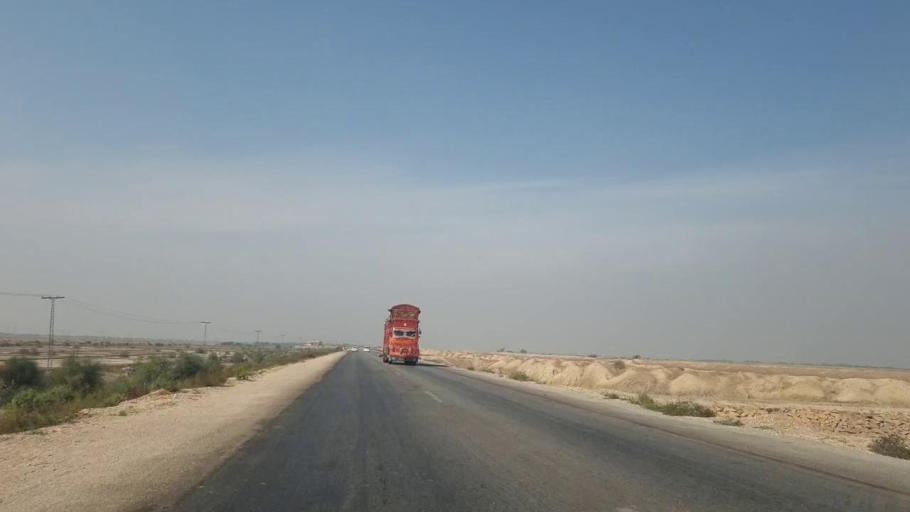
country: PK
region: Sindh
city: Sann
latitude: 25.9259
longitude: 68.2134
